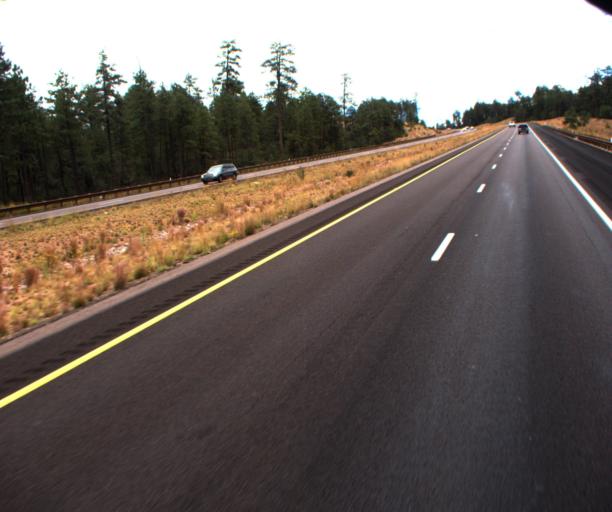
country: US
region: Arizona
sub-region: Gila County
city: Star Valley
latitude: 34.2944
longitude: -111.1285
